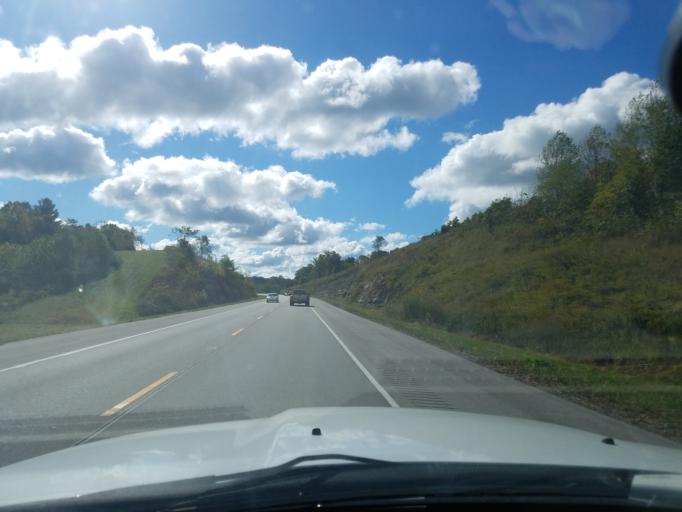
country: US
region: Kentucky
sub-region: Rockcastle County
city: Brodhead
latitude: 37.3658
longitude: -84.4110
